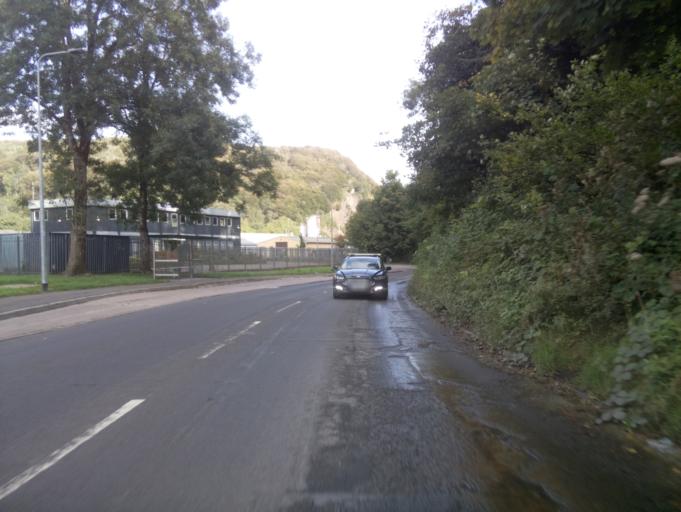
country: GB
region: Wales
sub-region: Cardiff
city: Radyr
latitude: 51.5388
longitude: -3.2665
